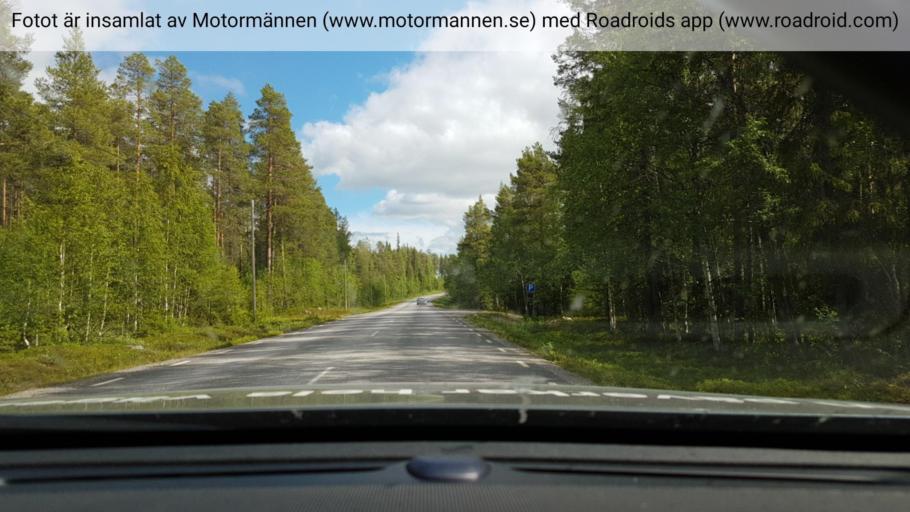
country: SE
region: Vaesterbotten
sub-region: Sorsele Kommun
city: Sorsele
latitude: 65.6620
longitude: 17.4155
